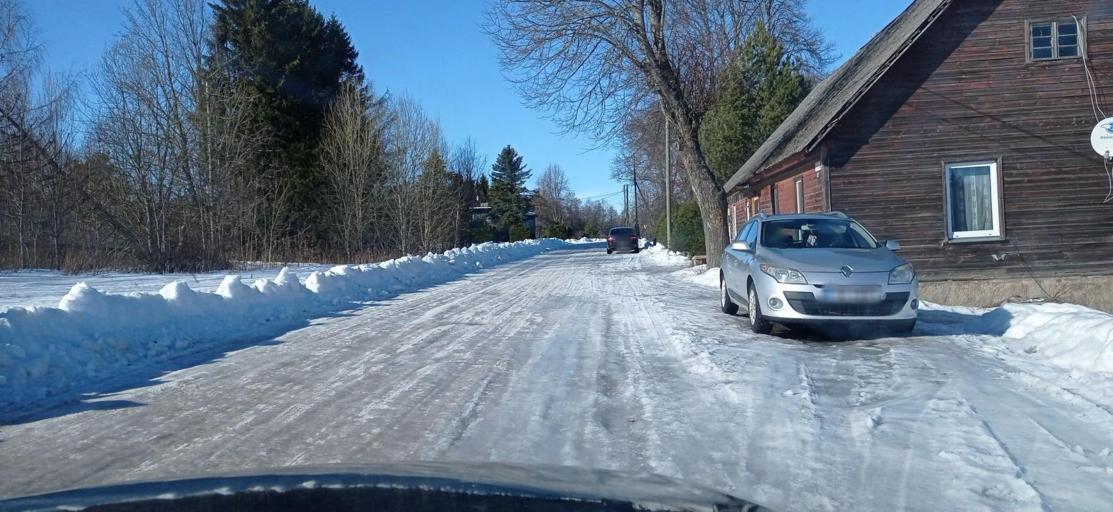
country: EE
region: Tartu
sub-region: Alatskivi vald
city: Kallaste
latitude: 58.6692
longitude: 27.1620
